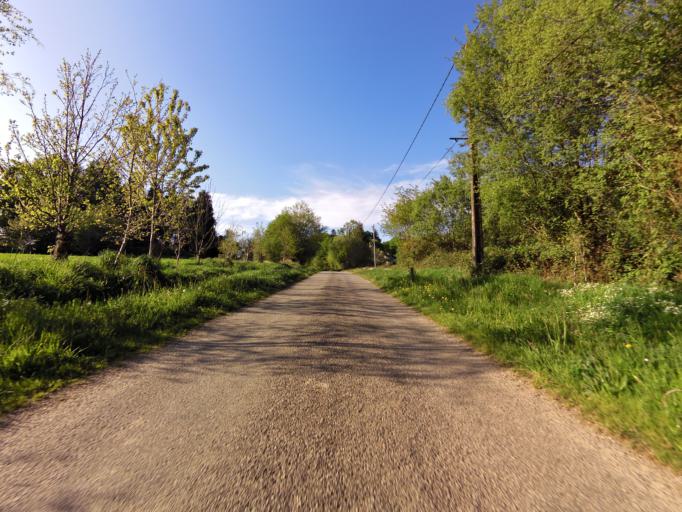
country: FR
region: Brittany
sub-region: Departement du Morbihan
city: Molac
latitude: 47.7339
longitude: -2.4761
